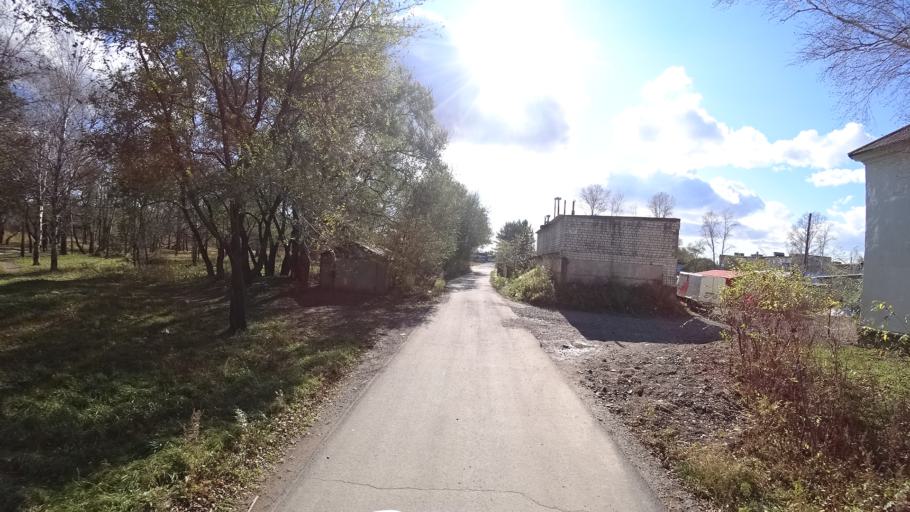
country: RU
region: Khabarovsk Krai
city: Amursk
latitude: 50.0997
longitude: 136.5034
